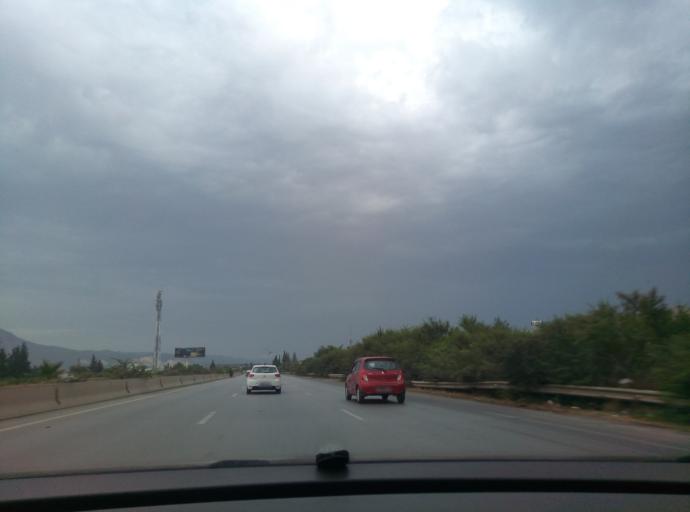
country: TN
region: Tunis
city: La Sebala du Mornag
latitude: 36.7198
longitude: 10.2644
